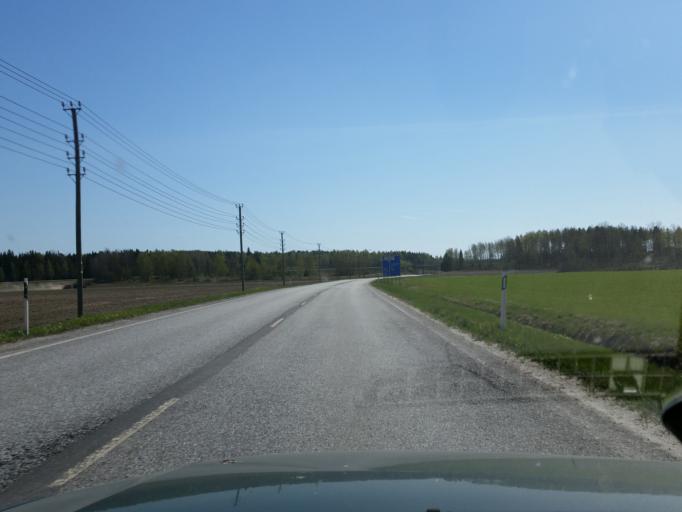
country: FI
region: Uusimaa
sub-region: Raaseporin
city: Inga
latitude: 60.0559
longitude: 23.9488
